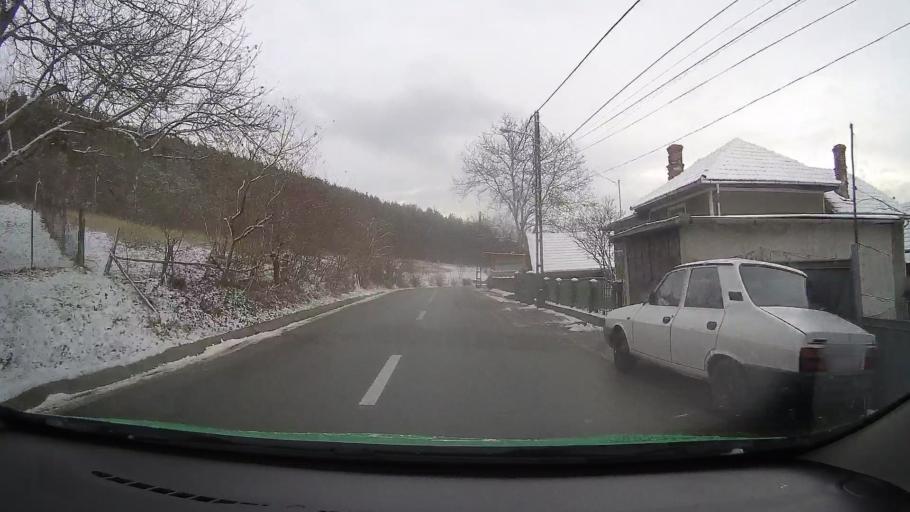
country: RO
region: Hunedoara
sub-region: Oras Hateg
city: Hateg
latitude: 45.6263
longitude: 22.9347
